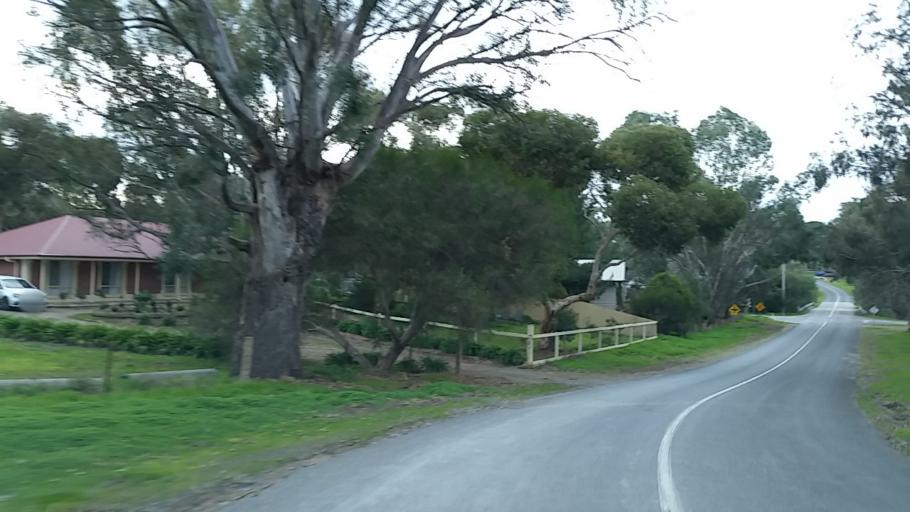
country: AU
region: South Australia
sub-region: Mount Barker
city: Nairne
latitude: -34.9513
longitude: 139.0129
